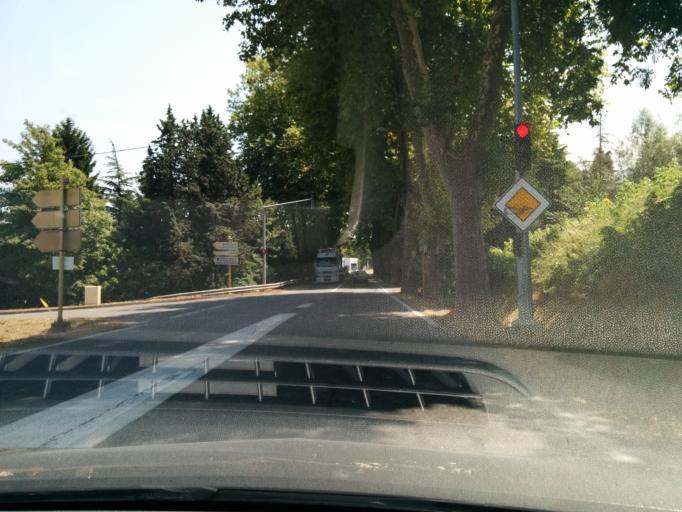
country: FR
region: Midi-Pyrenees
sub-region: Departement de la Haute-Garonne
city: Montgiscard
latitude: 43.4636
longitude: 1.5682
